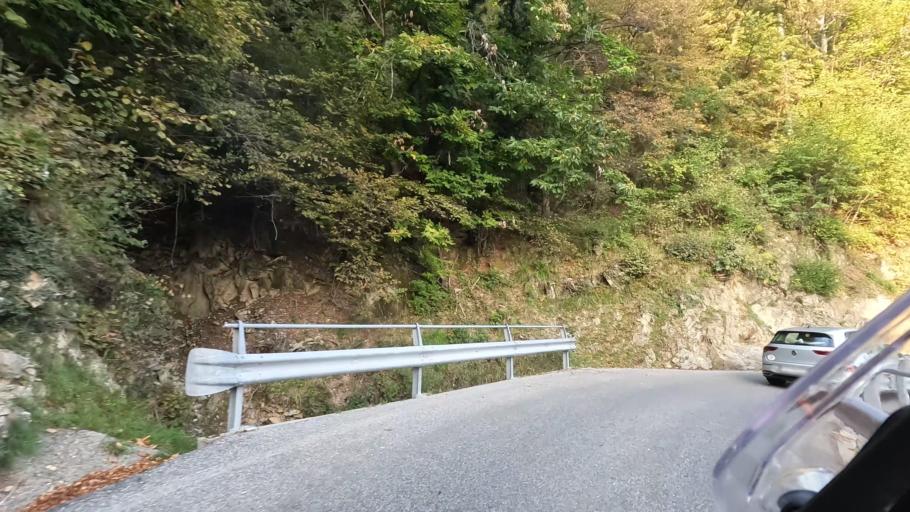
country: IT
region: Lombardy
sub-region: Provincia di Como
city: Pigra
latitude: 45.9556
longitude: 9.1211
